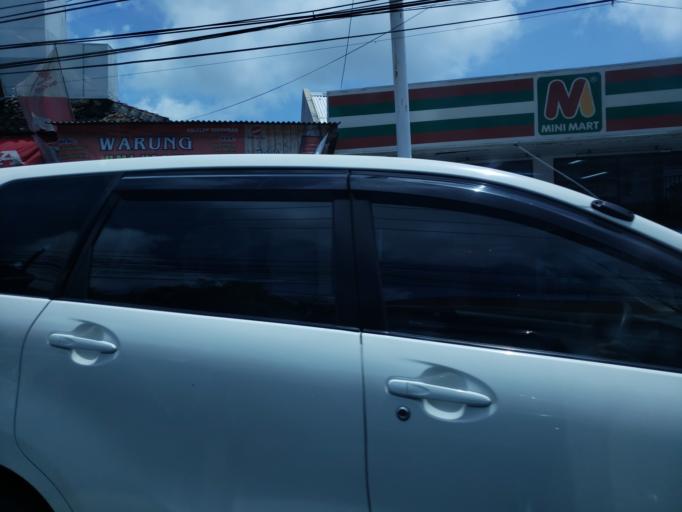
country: ID
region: Bali
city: Jimbaran
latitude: -8.8166
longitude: 115.1552
